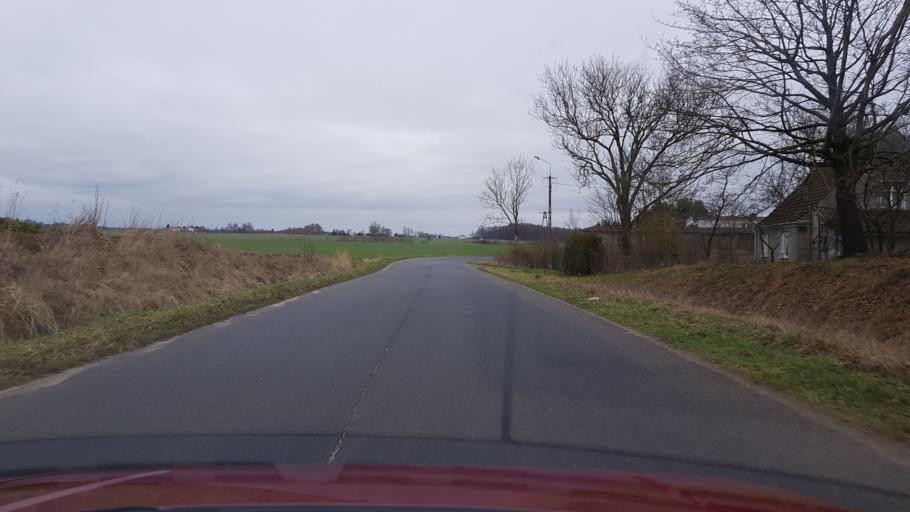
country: PL
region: West Pomeranian Voivodeship
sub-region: Powiat koszalinski
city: Mielno
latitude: 54.1778
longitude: 16.0104
